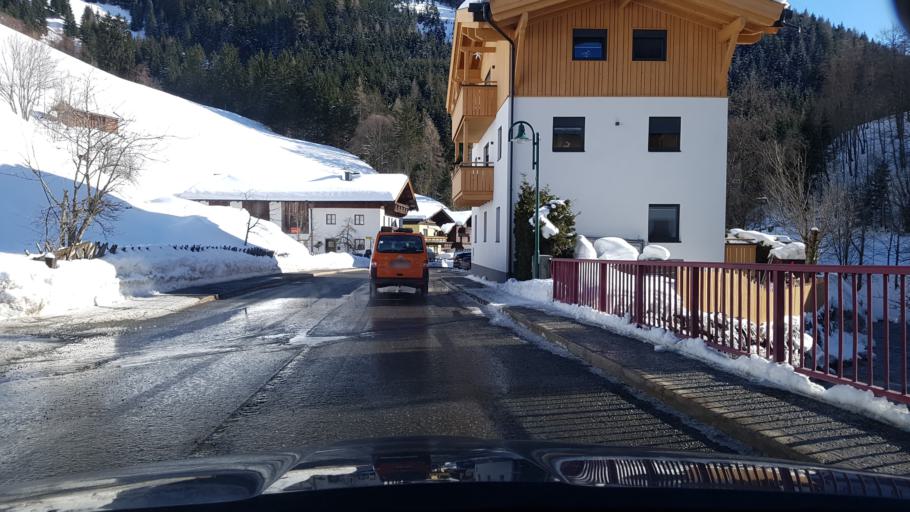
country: AT
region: Salzburg
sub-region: Politischer Bezirk Zell am See
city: Dienten am Hochkonig
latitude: 47.3797
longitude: 13.0015
